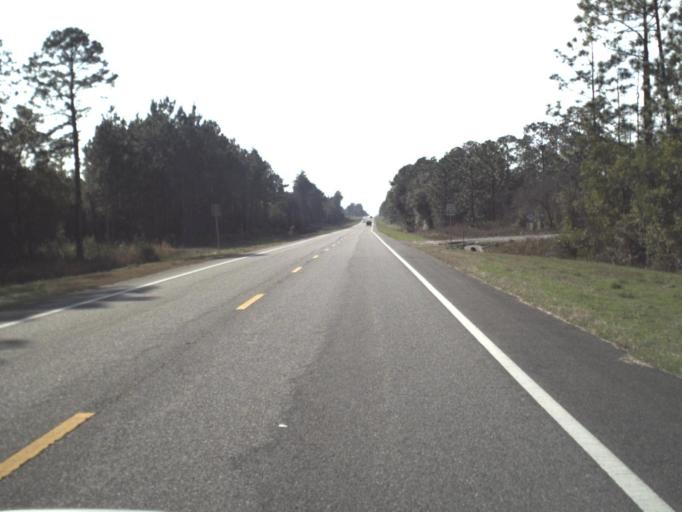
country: US
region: Florida
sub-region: Bay County
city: Youngstown
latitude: 30.4357
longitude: -85.4351
